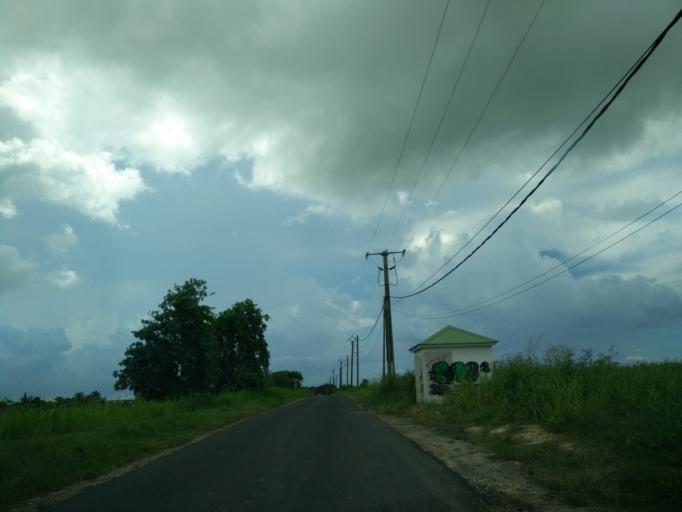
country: GP
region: Guadeloupe
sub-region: Guadeloupe
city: Le Moule
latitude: 16.2803
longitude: -61.3440
